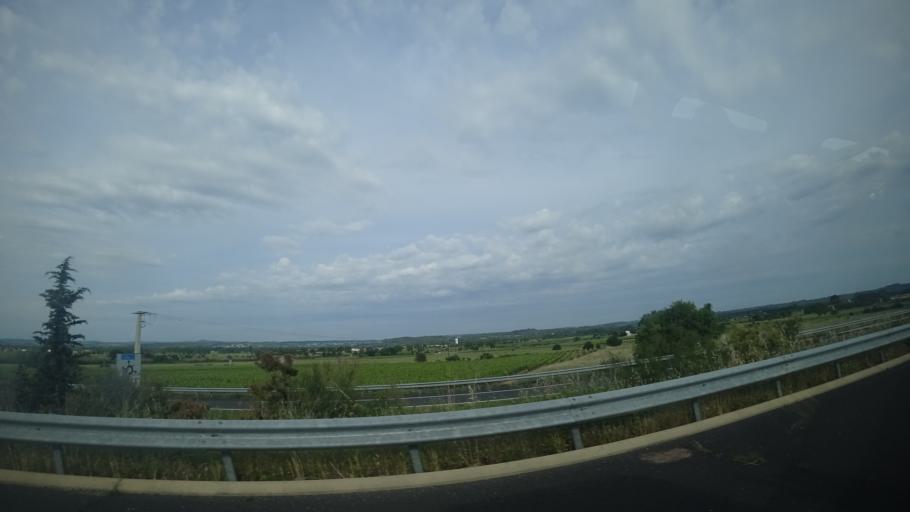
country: FR
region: Languedoc-Roussillon
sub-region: Departement de l'Herault
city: Paulhan
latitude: 43.5208
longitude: 3.4436
